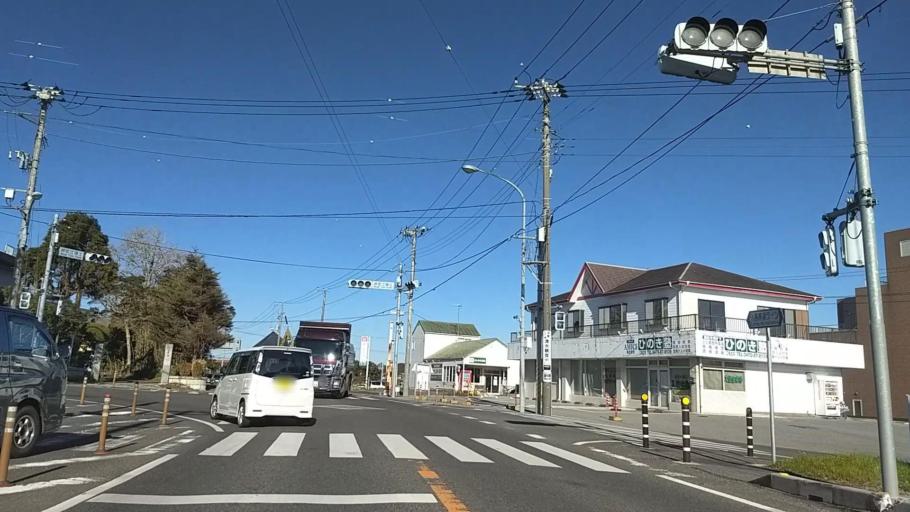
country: JP
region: Chiba
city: Ohara
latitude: 35.2925
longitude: 140.3951
